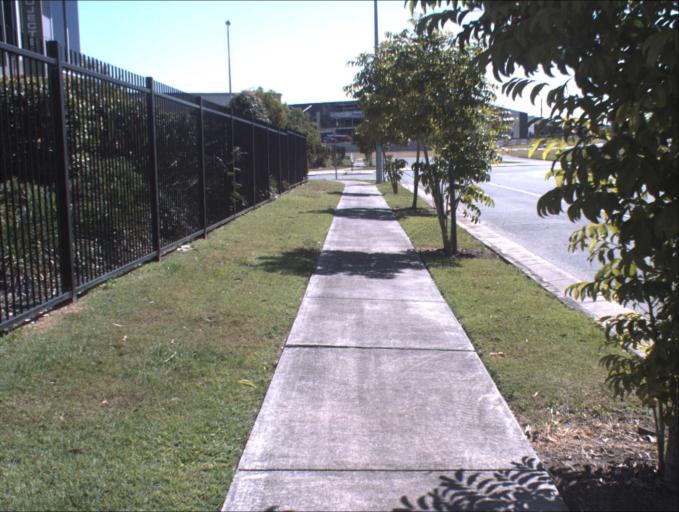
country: AU
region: Queensland
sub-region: Logan
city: Woodridge
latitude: -27.6533
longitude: 153.0755
